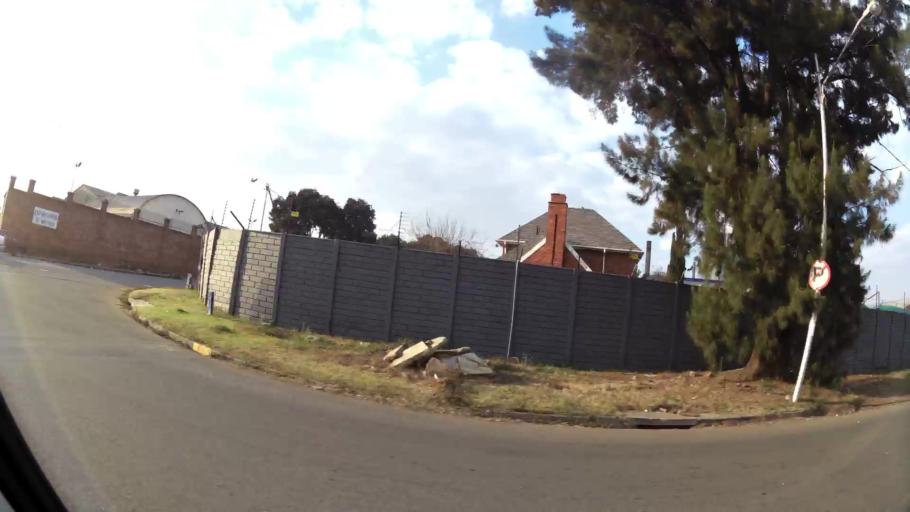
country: ZA
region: Gauteng
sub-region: Ekurhuleni Metropolitan Municipality
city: Germiston
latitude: -26.2585
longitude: 28.1838
